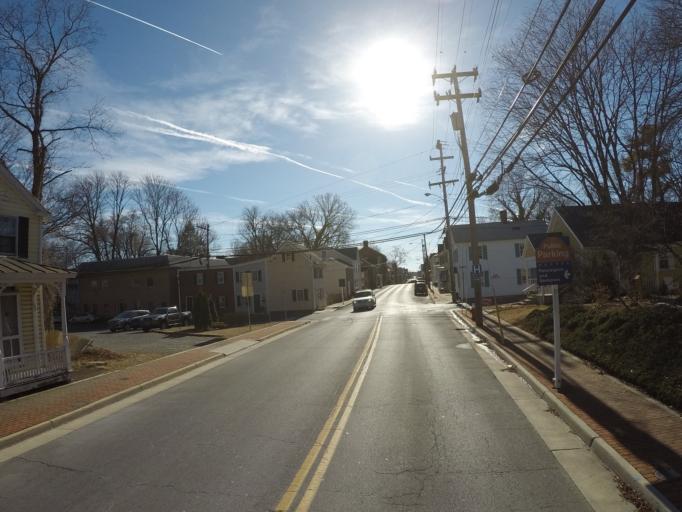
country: US
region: Virginia
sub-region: Loudoun County
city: Leesburg
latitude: 39.1176
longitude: -77.5636
